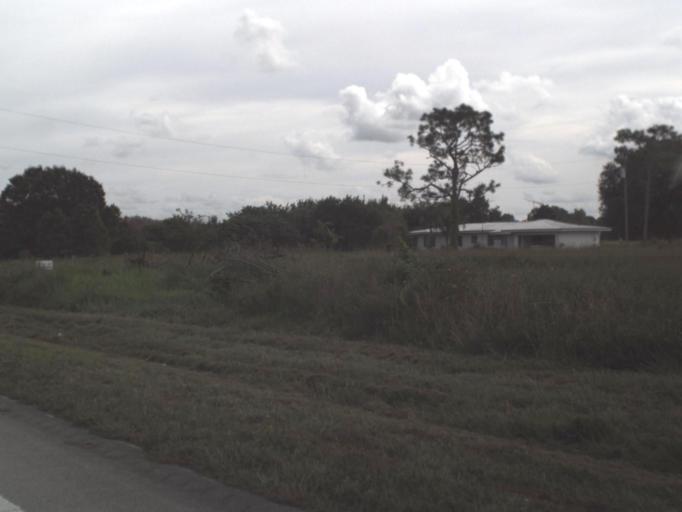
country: US
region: Florida
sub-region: Okeechobee County
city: Taylor Creek
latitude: 27.2722
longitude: -80.7263
